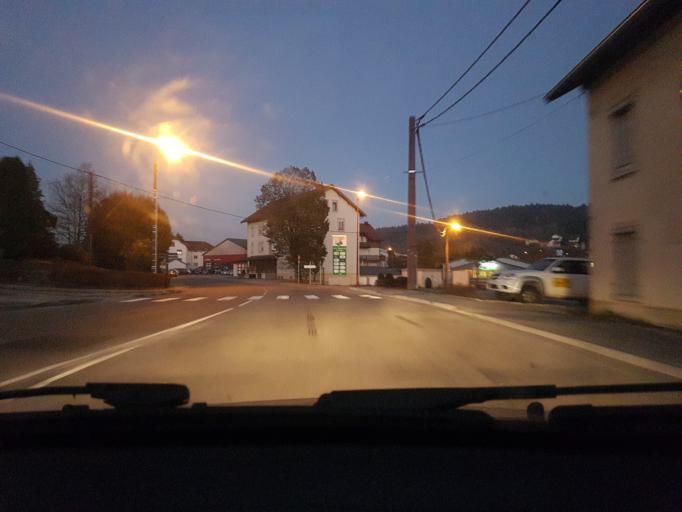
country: FR
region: Franche-Comte
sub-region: Departement du Doubs
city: Les Fins
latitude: 47.0827
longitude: 6.6346
